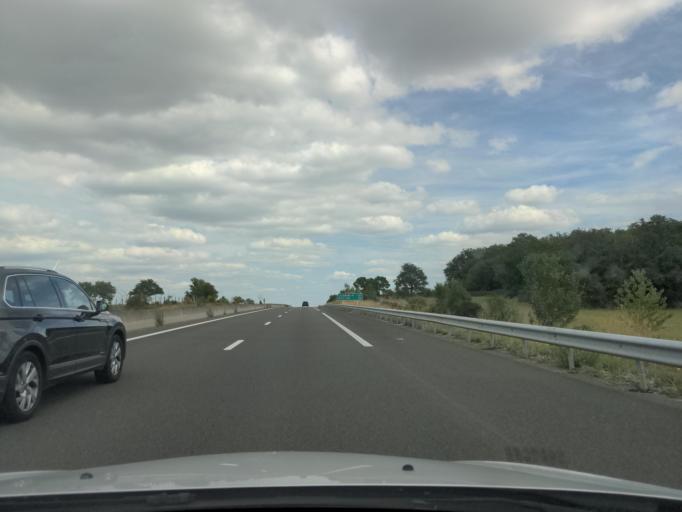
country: FR
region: Auvergne
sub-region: Departement de l'Allier
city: Quinssaines
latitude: 46.3073
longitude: 2.4546
